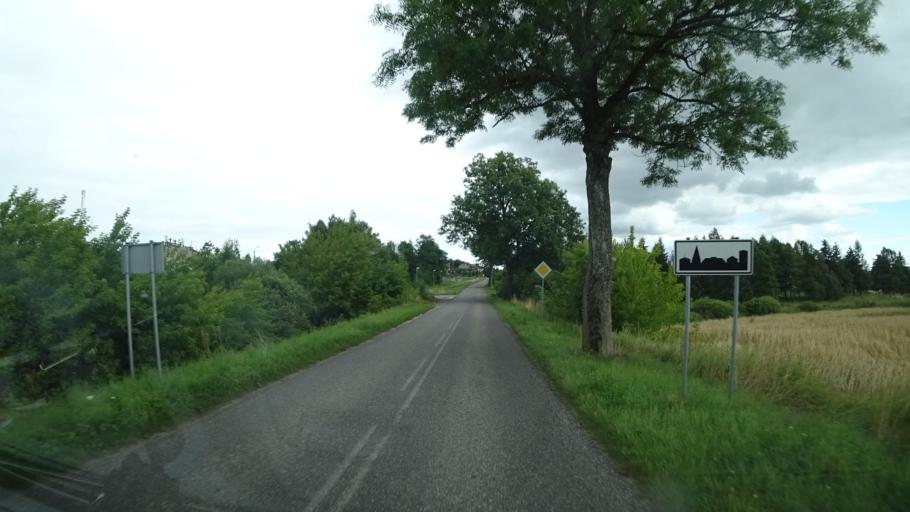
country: PL
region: Warmian-Masurian Voivodeship
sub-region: Powiat goldapski
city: Goldap
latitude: 54.3058
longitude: 22.4192
